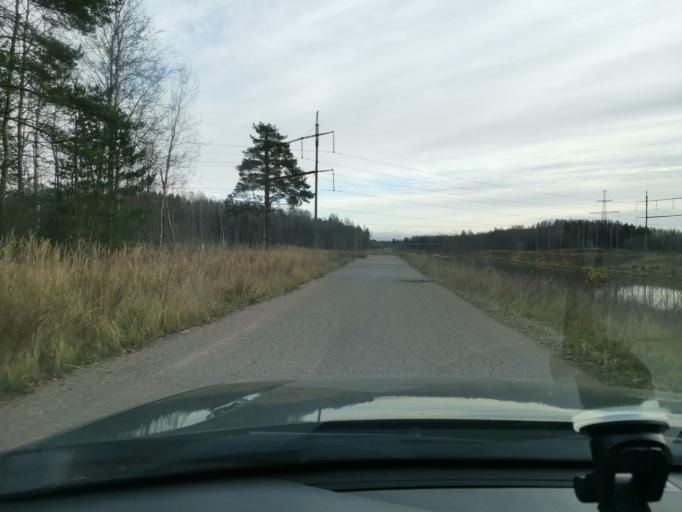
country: EE
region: Ida-Virumaa
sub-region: Sillamaee linn
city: Sillamae
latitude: 59.2639
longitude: 27.9023
